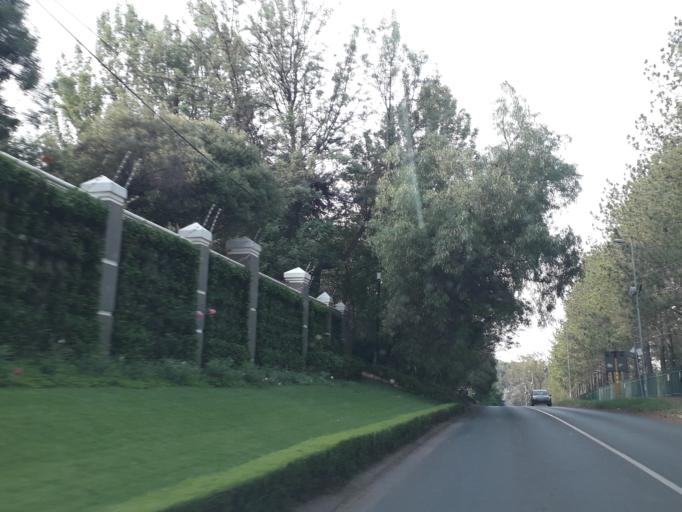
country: ZA
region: Gauteng
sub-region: City of Johannesburg Metropolitan Municipality
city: Johannesburg
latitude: -26.0837
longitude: 28.0408
